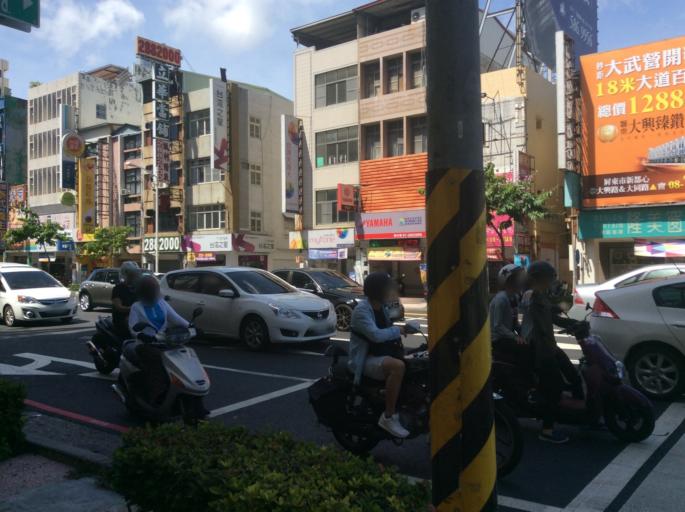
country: TW
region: Kaohsiung
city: Kaohsiung
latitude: 22.6328
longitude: 120.2946
